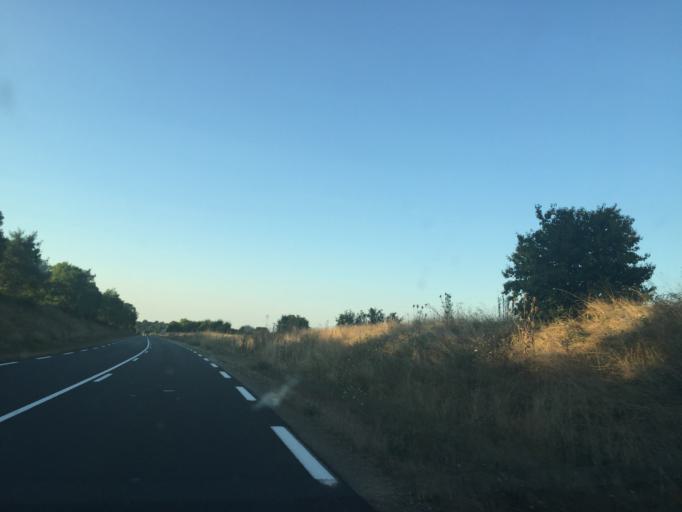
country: FR
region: Poitou-Charentes
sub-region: Departement de la Vienne
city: Lusignan
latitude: 46.4357
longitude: 0.1376
